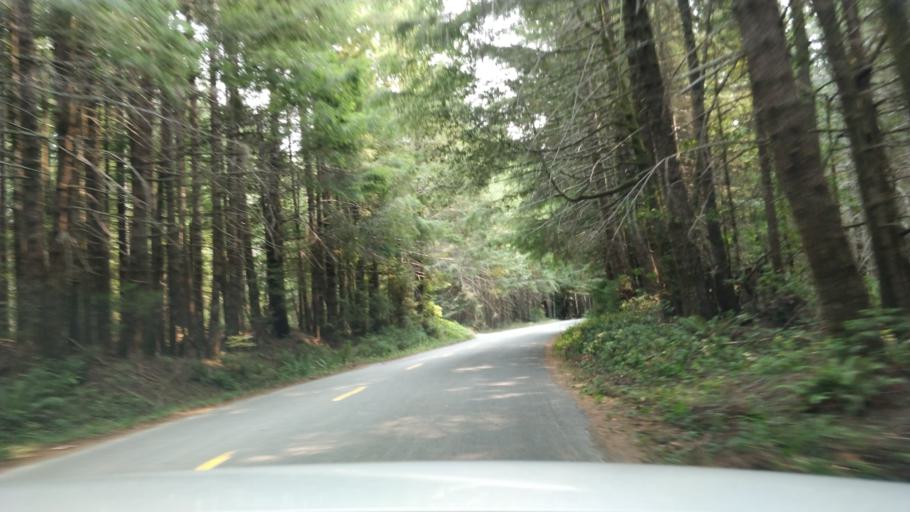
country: US
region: California
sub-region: Humboldt County
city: Westhaven-Moonstone
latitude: 41.2488
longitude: -123.9839
